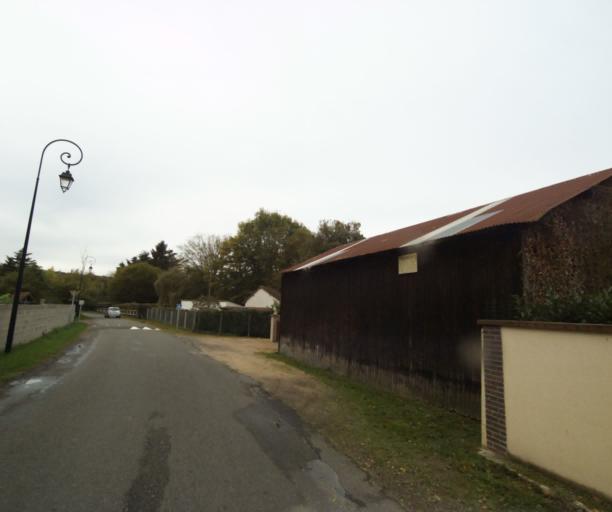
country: FR
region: Centre
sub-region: Departement d'Eure-et-Loir
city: Vert-en-Drouais
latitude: 48.7656
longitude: 1.3267
